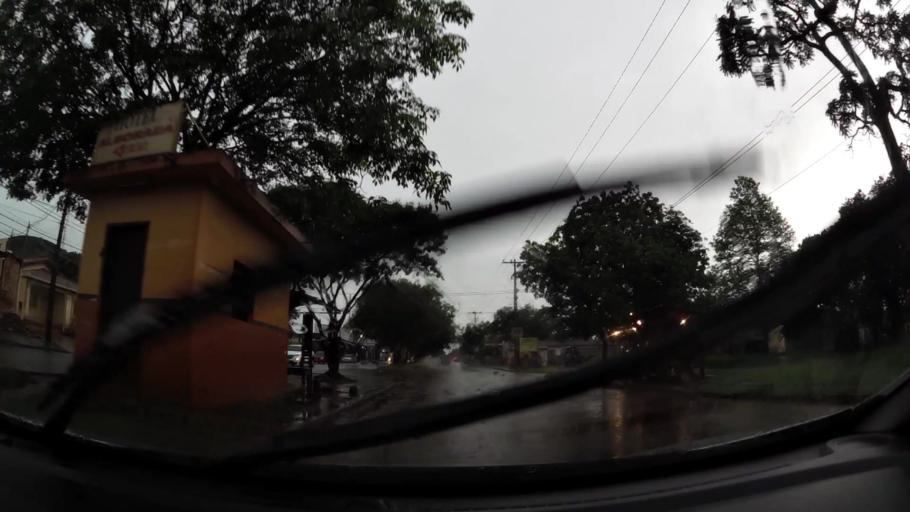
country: PY
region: Alto Parana
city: Presidente Franco
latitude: -25.5139
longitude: -54.6728
